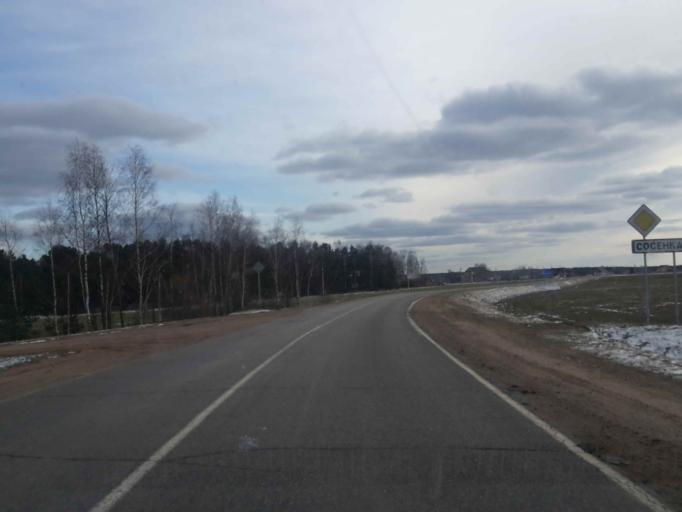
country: BY
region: Minsk
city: Il'ya
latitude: 54.5161
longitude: 27.2242
